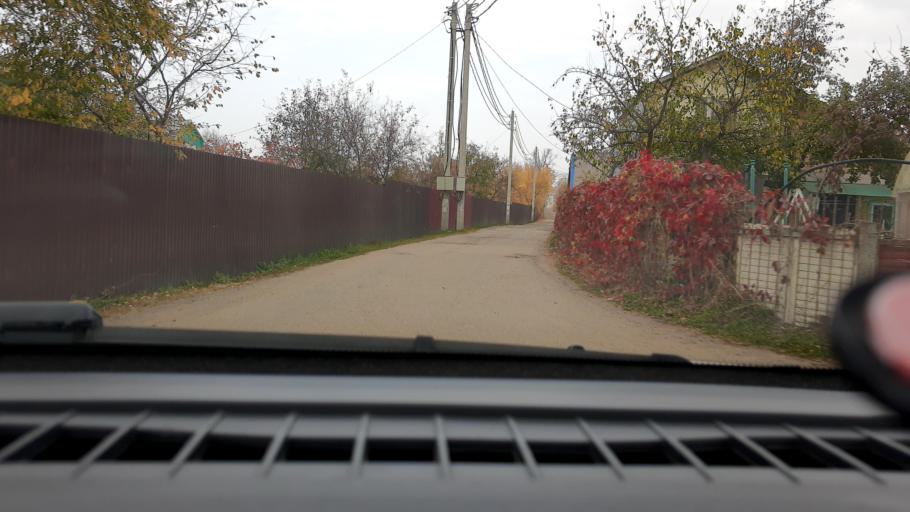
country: RU
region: Nizjnij Novgorod
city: Nizhniy Novgorod
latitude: 56.2707
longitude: 43.9571
